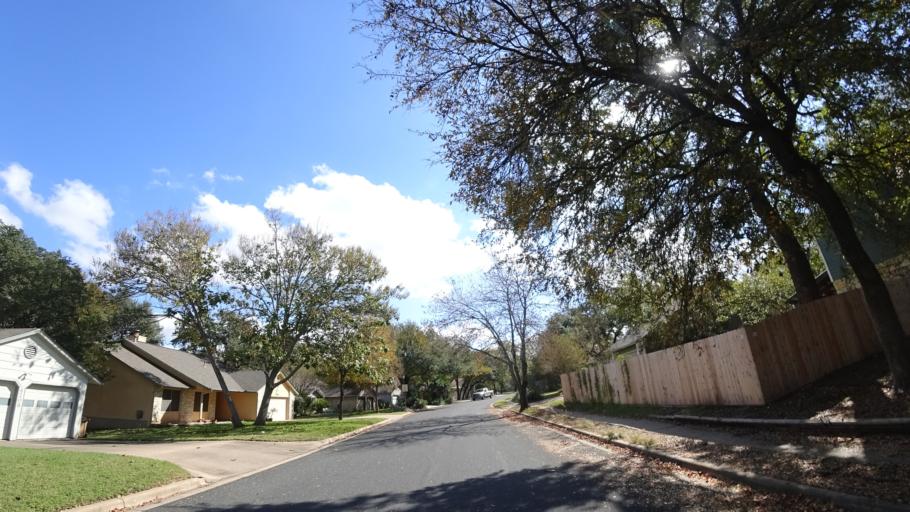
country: US
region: Texas
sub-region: Travis County
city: Wells Branch
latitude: 30.4218
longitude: -97.7219
